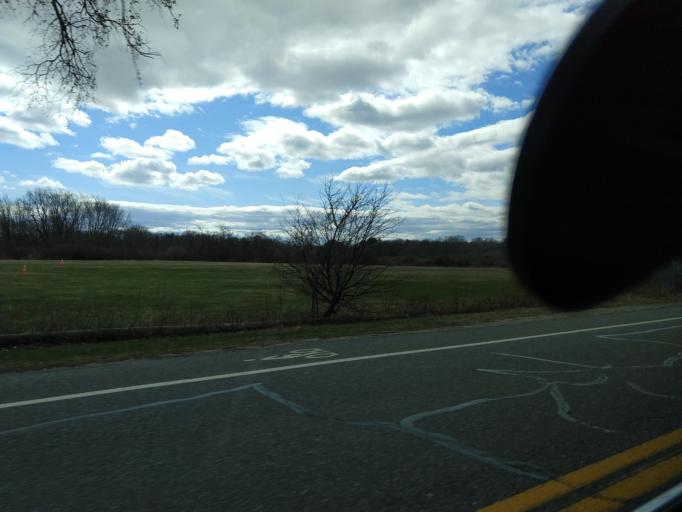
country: US
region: Massachusetts
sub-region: Essex County
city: Newburyport
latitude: 42.7979
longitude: -70.8453
